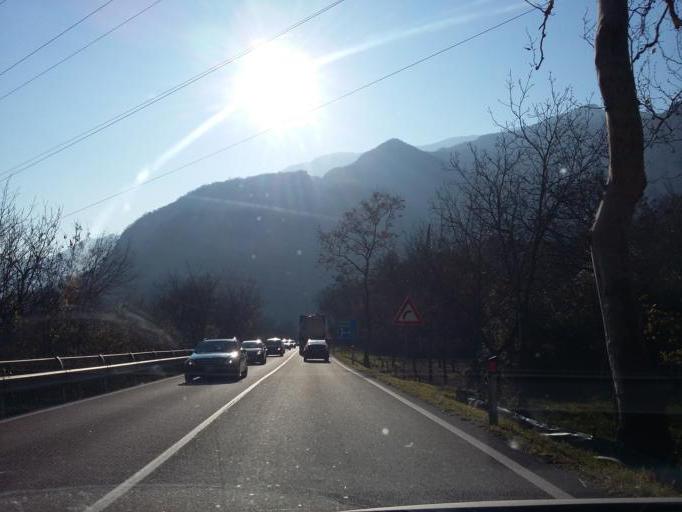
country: IT
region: Trentino-Alto Adige
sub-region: Provincia di Trento
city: Nago-Torbole
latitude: 45.8727
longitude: 10.9074
